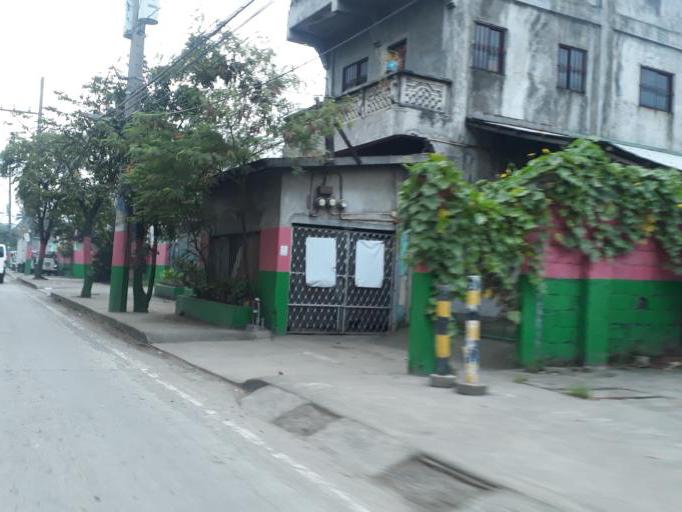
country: PH
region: Calabarzon
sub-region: Province of Rizal
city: Valenzuela
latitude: 14.6947
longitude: 120.9547
